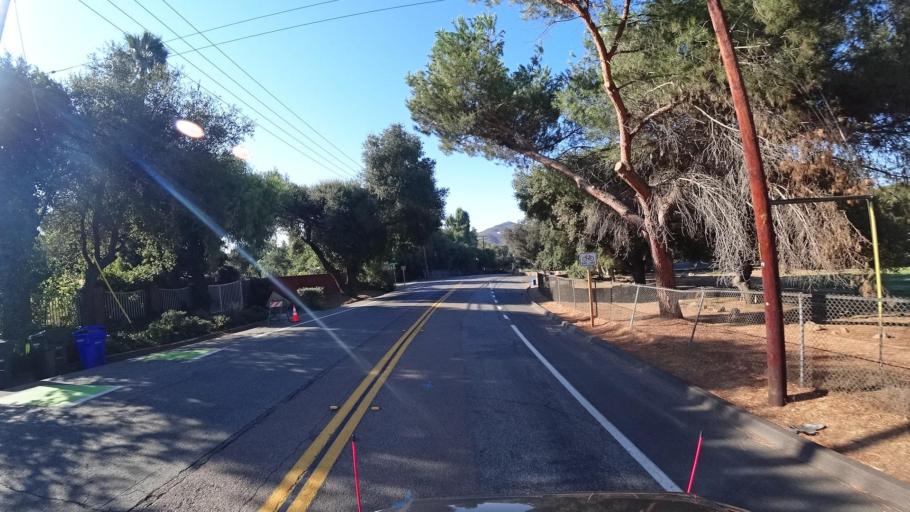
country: US
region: California
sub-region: San Diego County
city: Escondido
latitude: 33.0813
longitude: -117.0829
